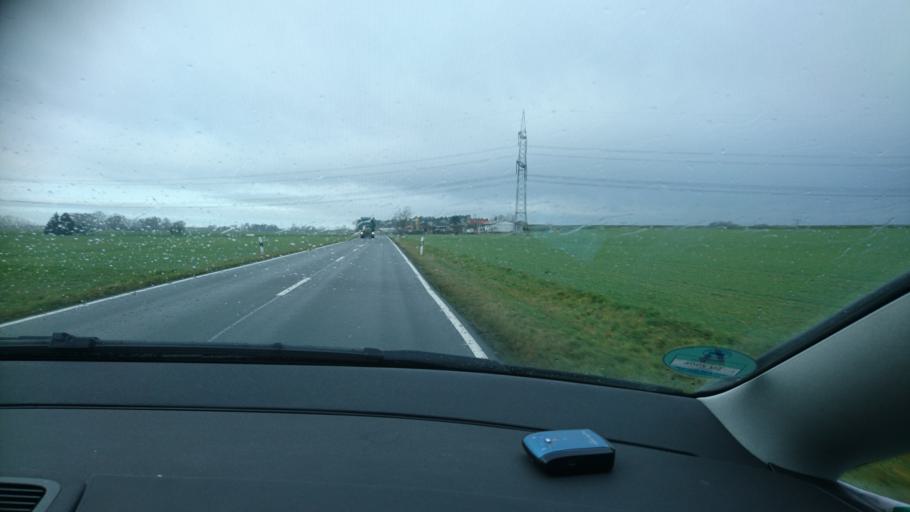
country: DE
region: Saxony
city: Laussig
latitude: 51.5802
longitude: 12.6401
